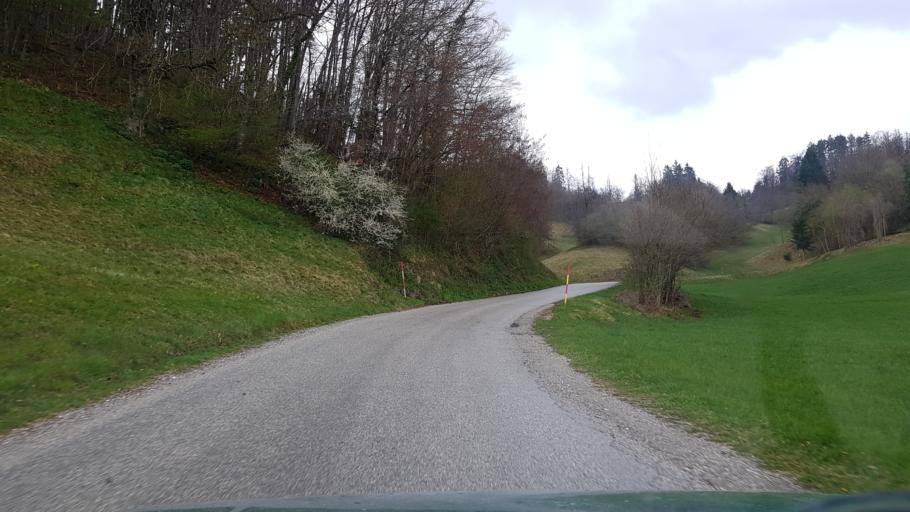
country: SI
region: Tolmin
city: Tolmin
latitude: 46.1116
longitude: 13.8382
